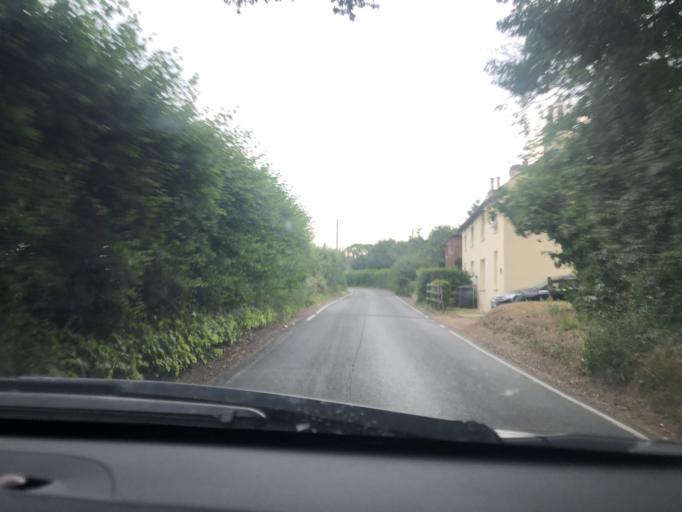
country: GB
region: England
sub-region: Kent
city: Sturry
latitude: 51.3253
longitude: 1.1450
